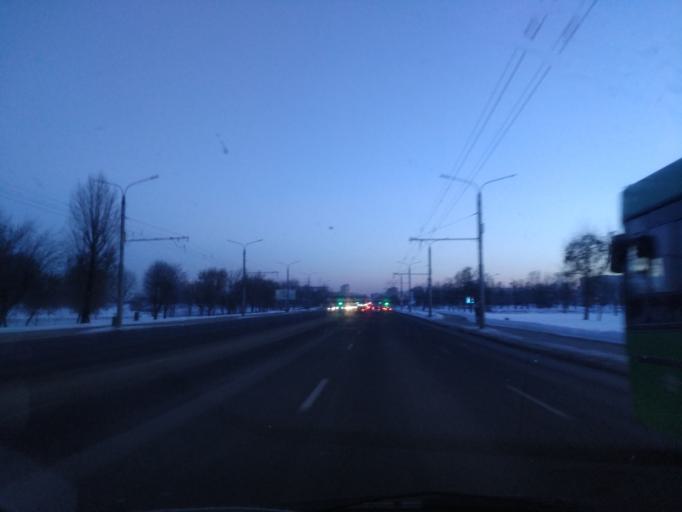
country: BY
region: Mogilev
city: Mahilyow
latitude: 53.8893
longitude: 30.3298
